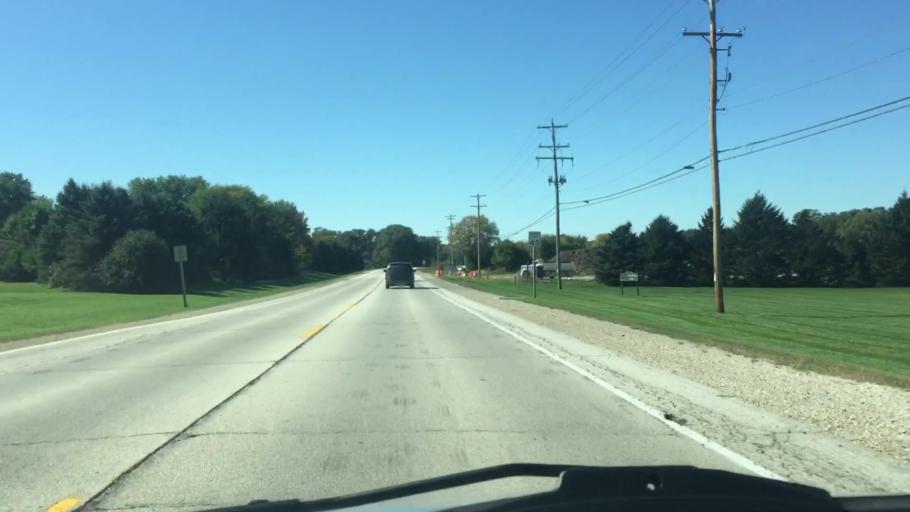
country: US
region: Wisconsin
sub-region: Waukesha County
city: Wales
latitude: 43.0166
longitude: -88.3696
